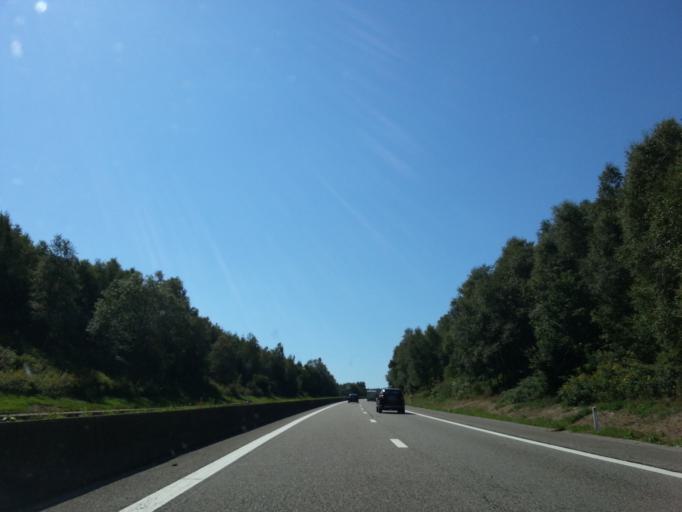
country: BE
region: Wallonia
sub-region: Province de Liege
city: Saint-Vith
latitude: 50.3353
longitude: 6.0901
